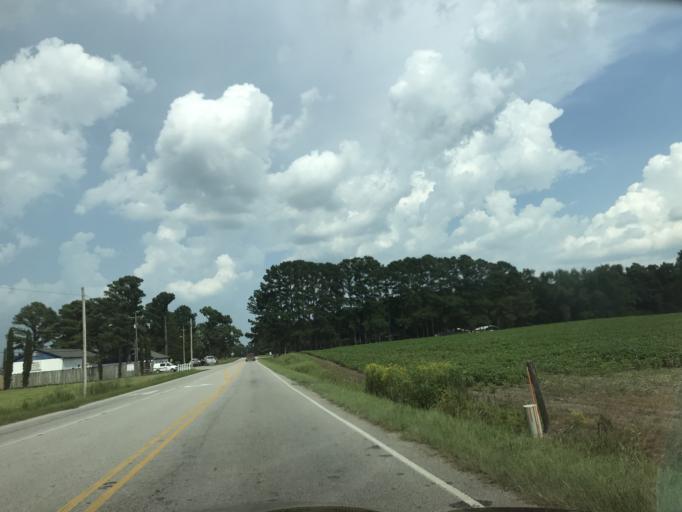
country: US
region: North Carolina
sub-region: Johnston County
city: Benson
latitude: 35.5142
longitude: -78.5433
